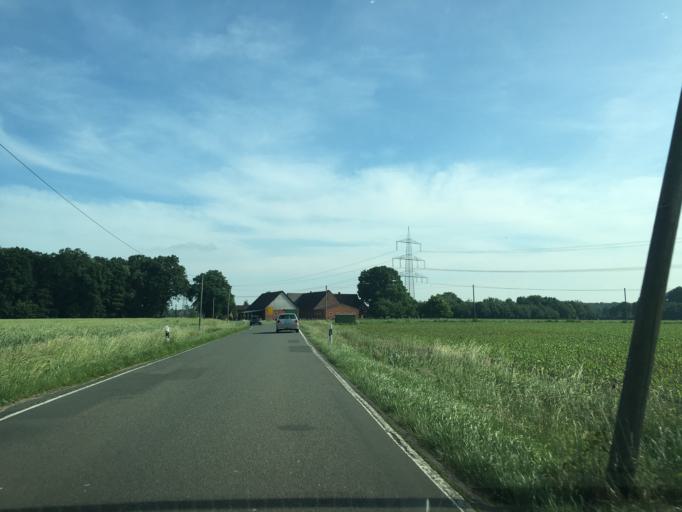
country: DE
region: North Rhine-Westphalia
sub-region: Regierungsbezirk Munster
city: Nordwalde
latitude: 52.1317
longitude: 7.4335
